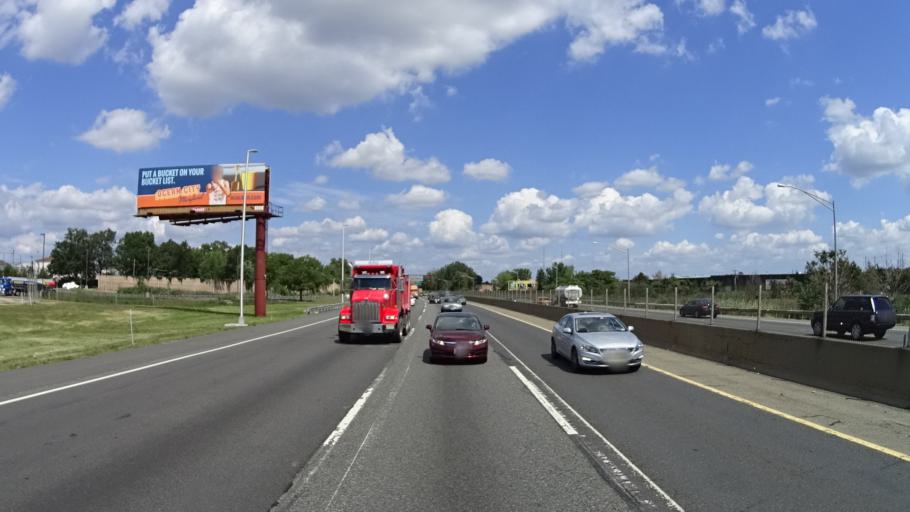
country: US
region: New Jersey
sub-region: Hudson County
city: Secaucus
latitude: 40.7689
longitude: -74.0642
